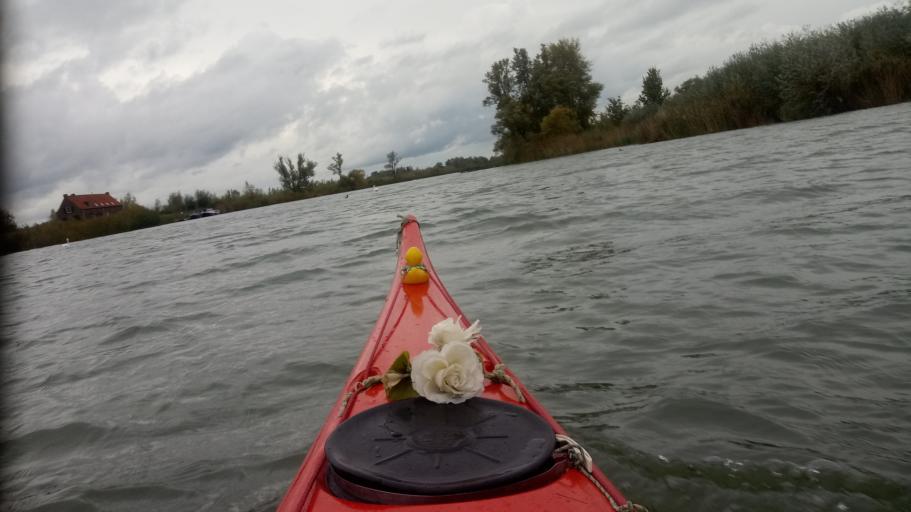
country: NL
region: South Holland
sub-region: Gemeente Sliedrecht
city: Sliedrecht
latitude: 51.7665
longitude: 4.7655
